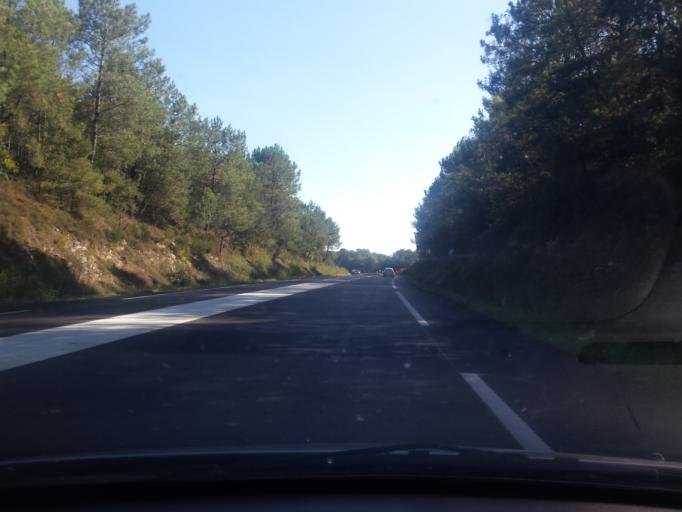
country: FR
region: Brittany
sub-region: Departement du Morbihan
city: Meucon
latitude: 47.7367
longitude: -2.7643
